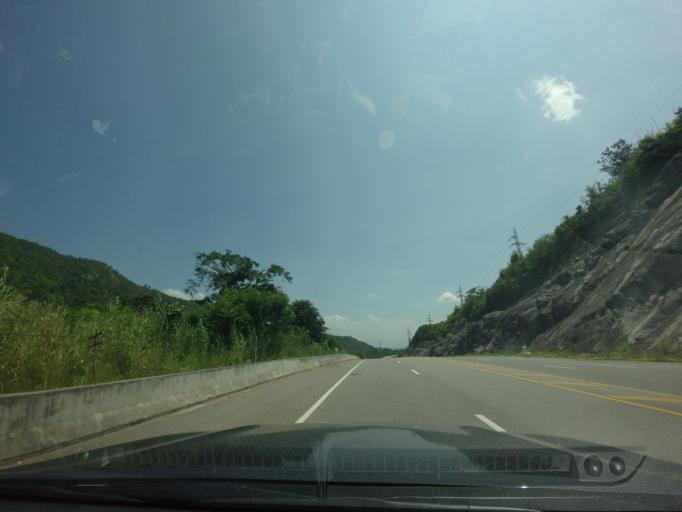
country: TH
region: Phetchabun
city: Lom Sak
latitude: 16.7732
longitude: 101.1320
